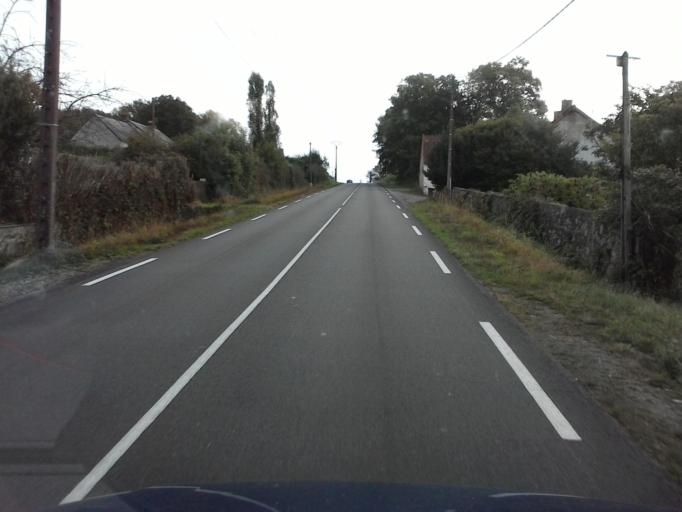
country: FR
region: Bourgogne
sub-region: Departement de Saone-et-Loire
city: Autun
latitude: 47.0047
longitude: 4.2004
